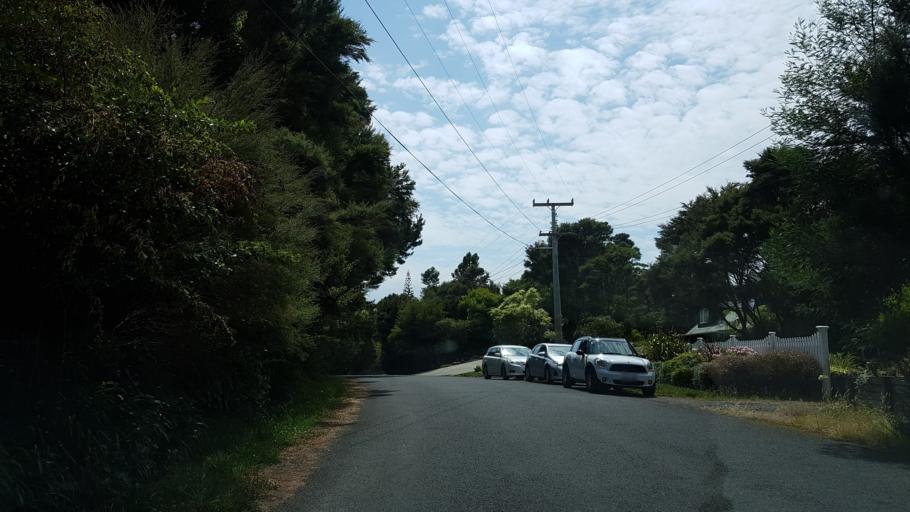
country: NZ
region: Auckland
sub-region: Auckland
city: North Shore
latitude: -36.7828
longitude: 174.6774
